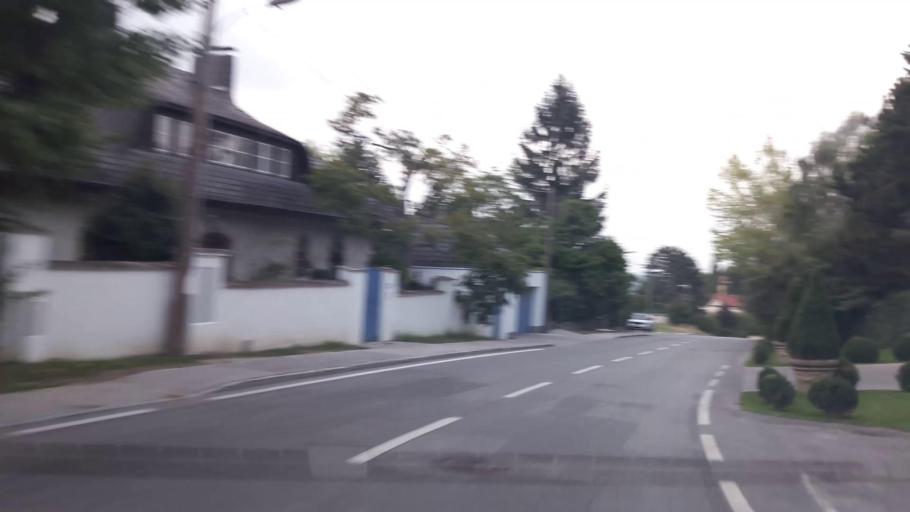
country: AT
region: Lower Austria
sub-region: Politischer Bezirk Wien-Umgebung
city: Klosterneuburg
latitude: 48.2893
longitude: 16.3260
